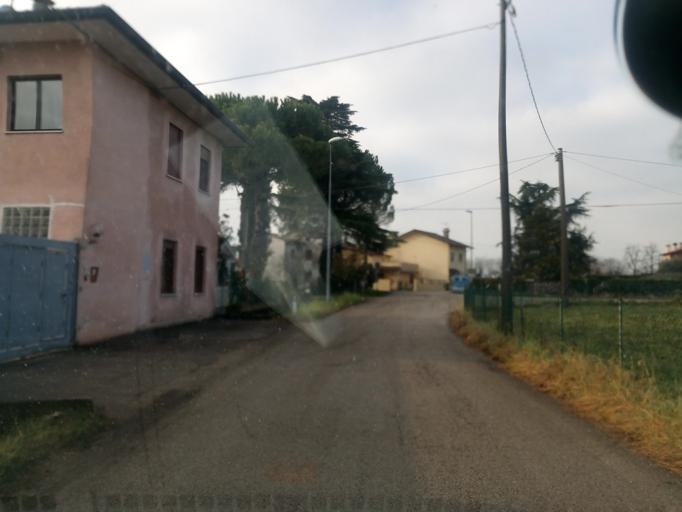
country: IT
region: Veneto
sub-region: Provincia di Vicenza
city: Montecchio Precalcino
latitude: 45.6836
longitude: 11.5794
